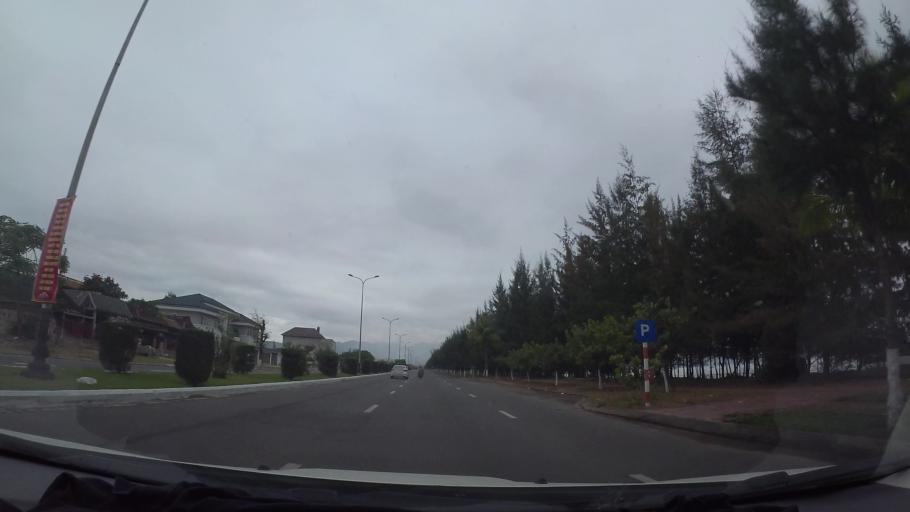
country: VN
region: Da Nang
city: Lien Chieu
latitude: 16.0996
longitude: 108.1415
